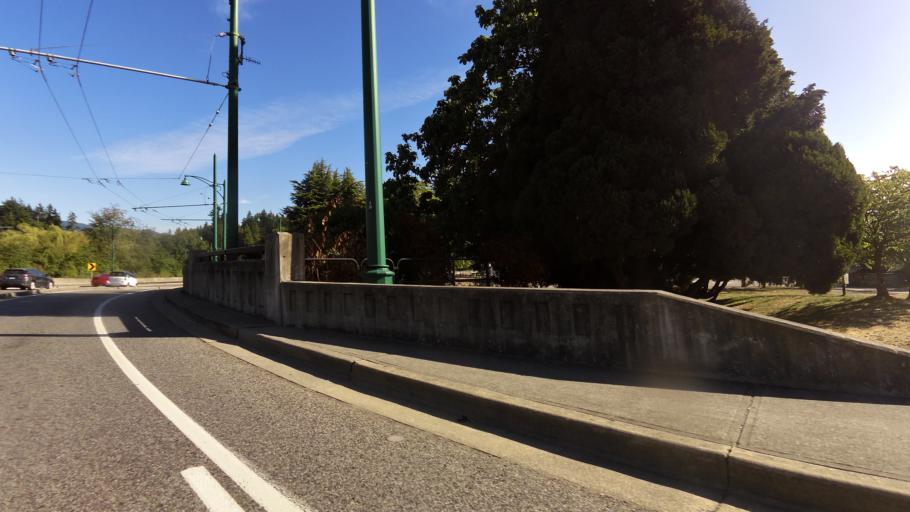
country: CA
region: British Columbia
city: West End
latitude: 49.2948
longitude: -123.1367
